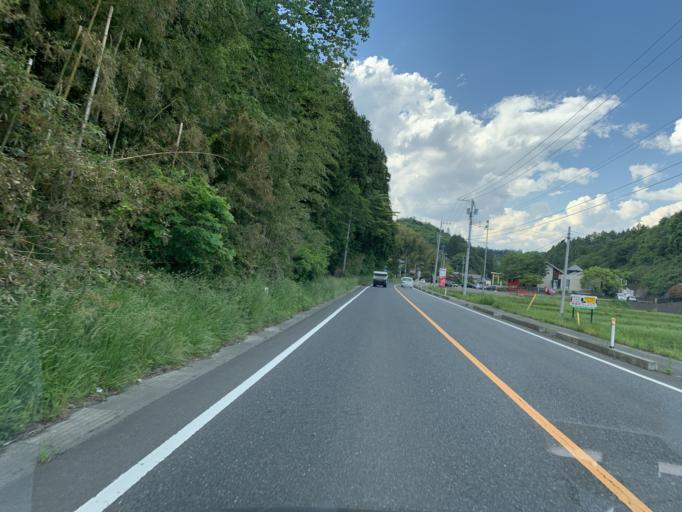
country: JP
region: Miyagi
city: Wakuya
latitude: 38.5556
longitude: 141.1372
